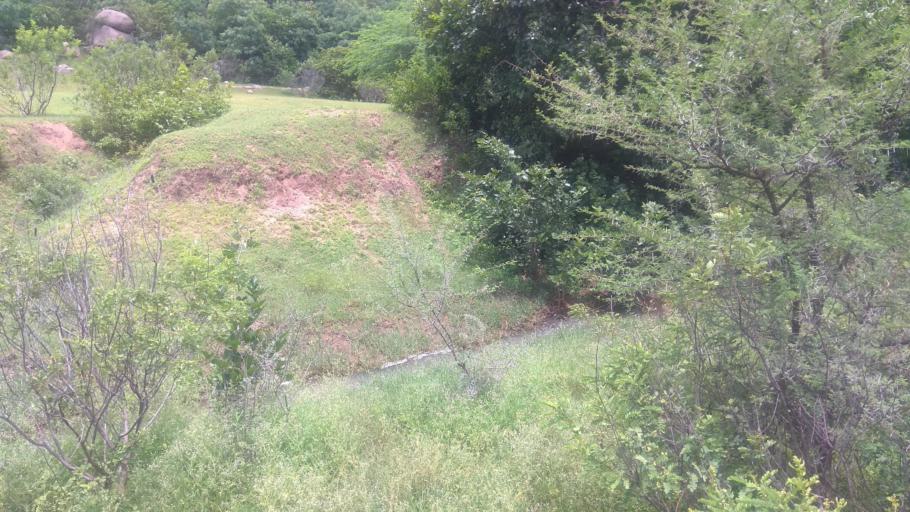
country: IN
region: Telangana
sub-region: Mahbubnagar
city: Farrukhnagar
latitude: 16.8901
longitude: 78.5016
